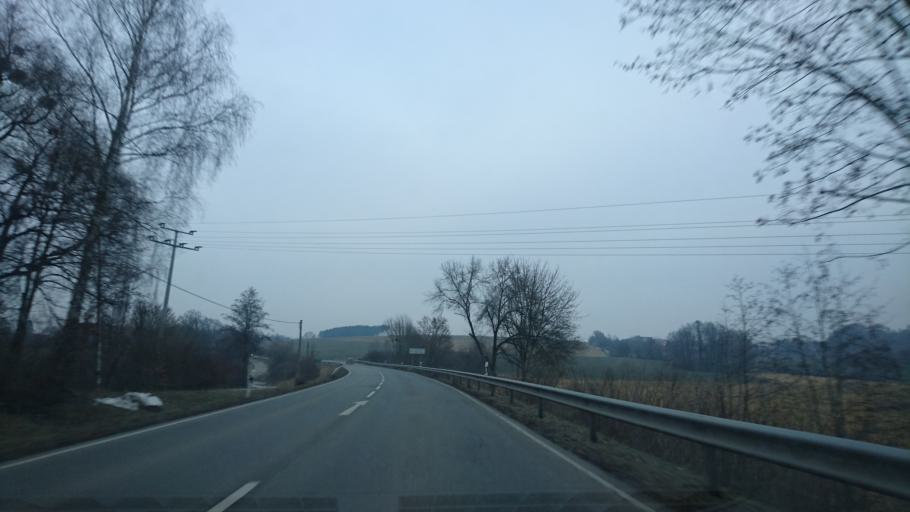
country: DE
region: Bavaria
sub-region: Lower Bavaria
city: Bad Griesbach
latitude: 48.4223
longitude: 13.1797
